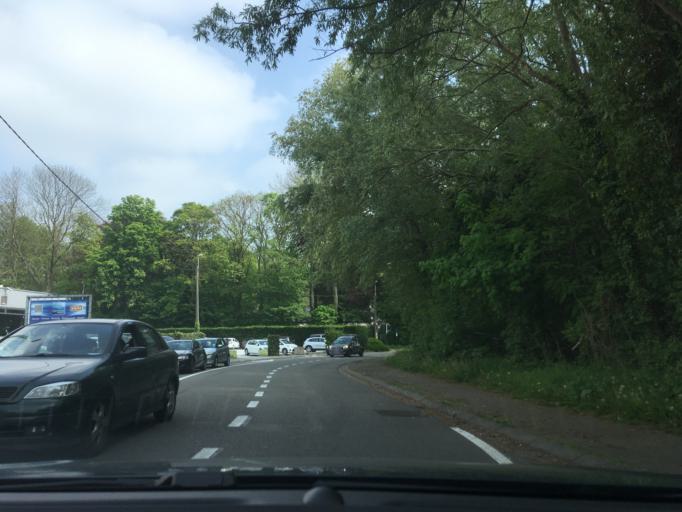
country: BE
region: Flanders
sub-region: Provincie Vlaams-Brabant
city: Dilbeek
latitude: 50.8598
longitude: 4.2789
